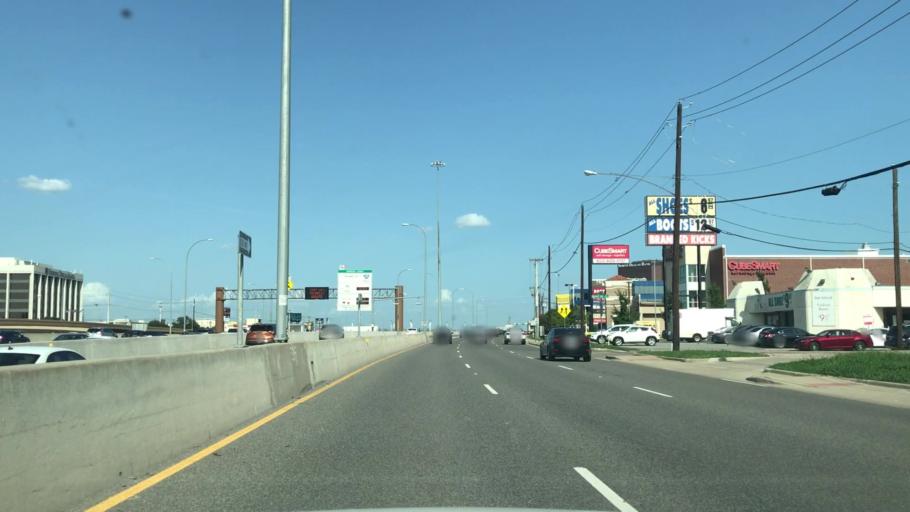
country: US
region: Texas
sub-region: Dallas County
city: Addison
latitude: 32.9256
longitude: -96.8082
